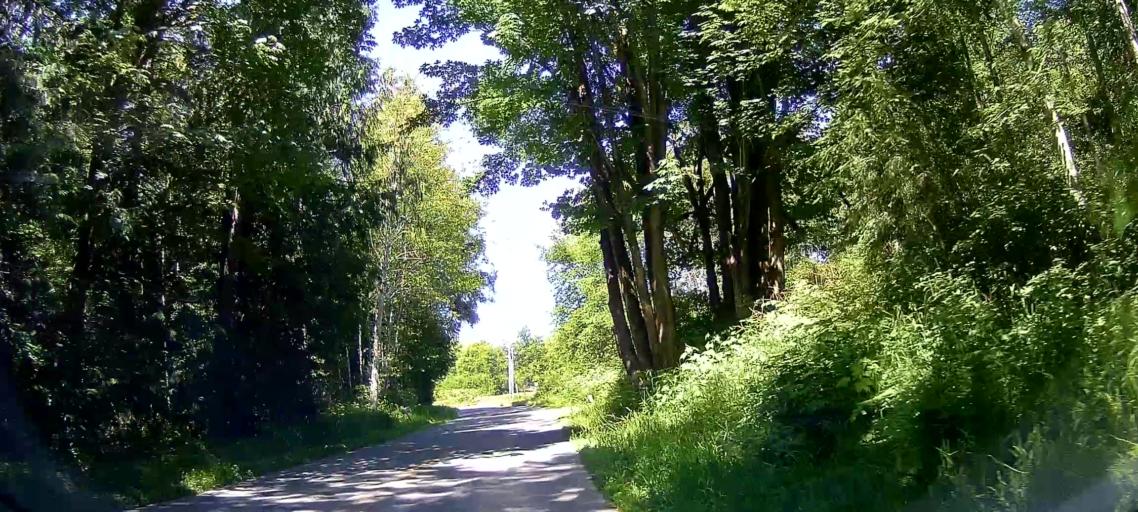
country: US
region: Washington
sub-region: Whatcom County
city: Sudden Valley
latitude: 48.6183
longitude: -122.3186
